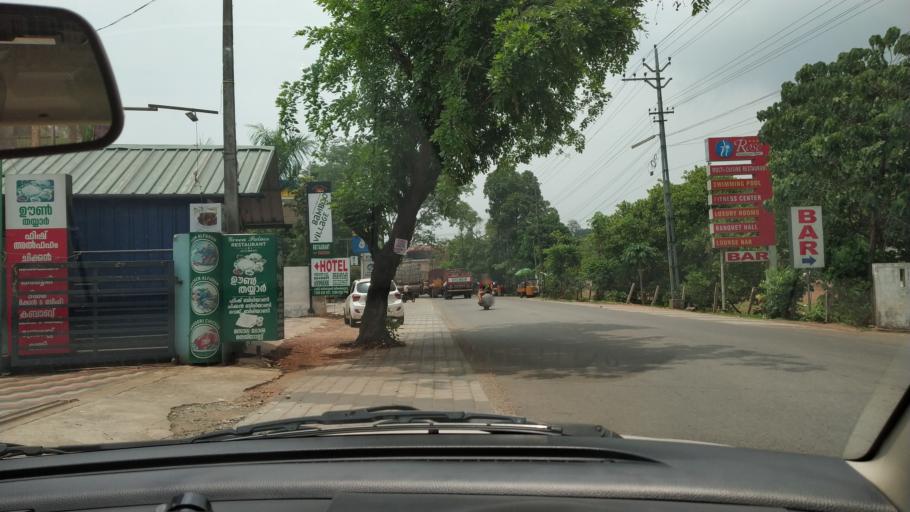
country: IN
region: Kerala
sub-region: Malappuram
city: Manjeri
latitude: 11.2689
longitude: 76.2152
